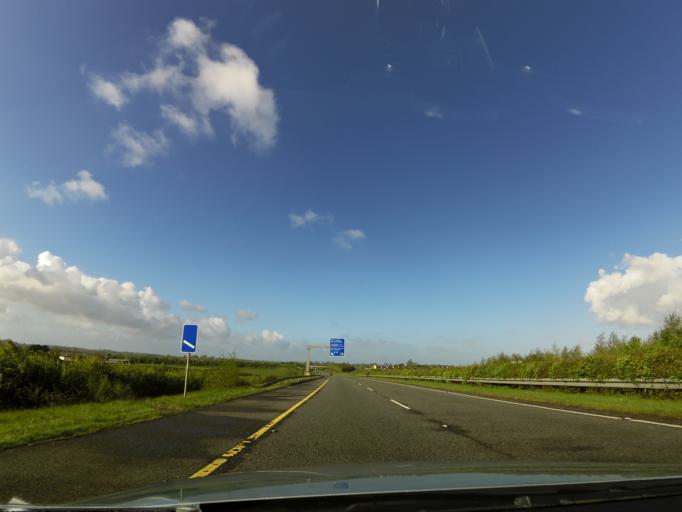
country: IE
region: Munster
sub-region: County Limerick
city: Annacotty
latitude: 52.6524
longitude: -8.5550
